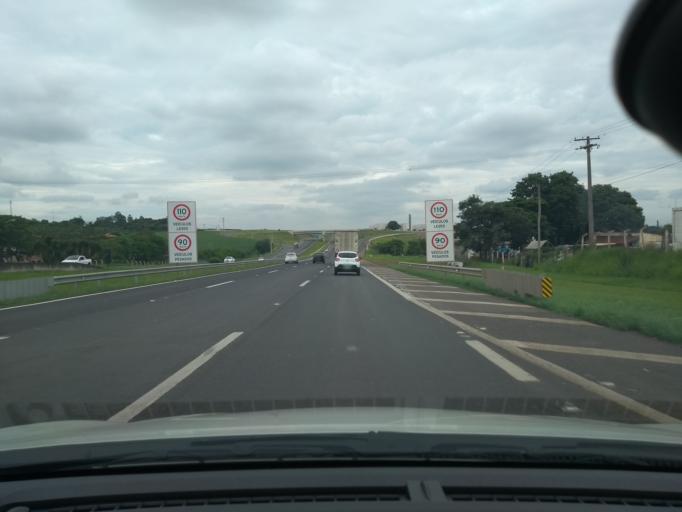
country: BR
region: Sao Paulo
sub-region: Araras
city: Araras
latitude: -22.3833
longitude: -47.3942
